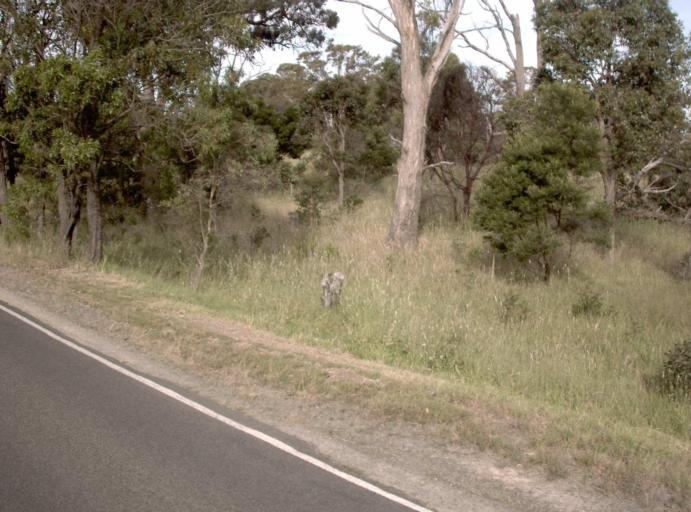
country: AU
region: Victoria
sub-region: Latrobe
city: Traralgon
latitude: -38.0639
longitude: 146.6196
